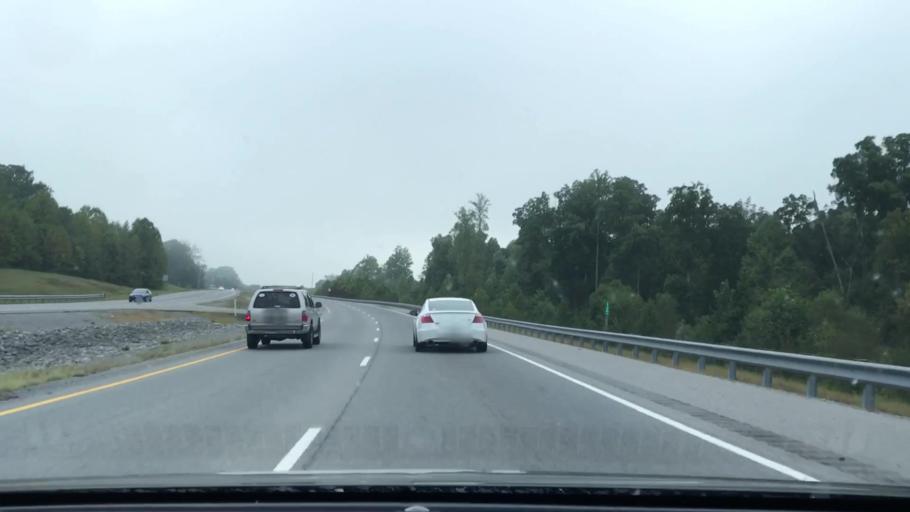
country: US
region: Tennessee
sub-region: Sumner County
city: Portland
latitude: 36.4866
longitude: -86.4849
